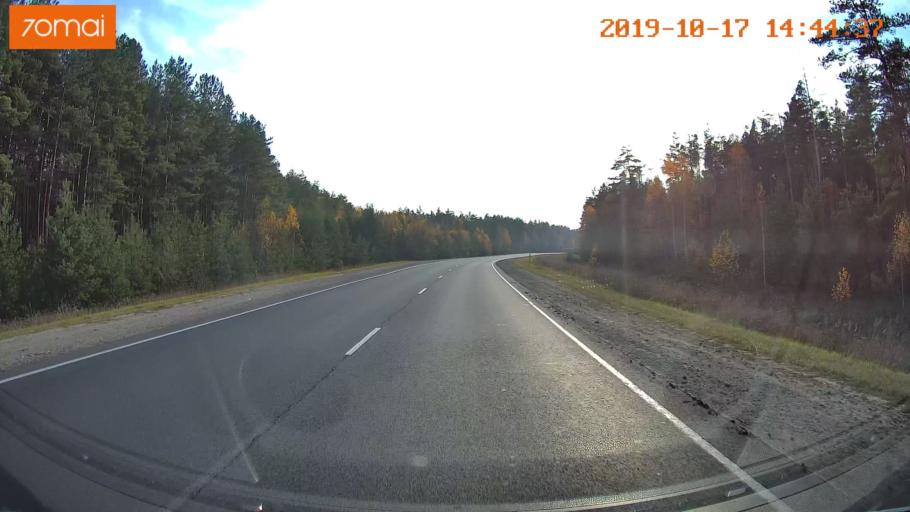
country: RU
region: Rjazan
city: Solotcha
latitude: 54.8103
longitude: 39.8897
